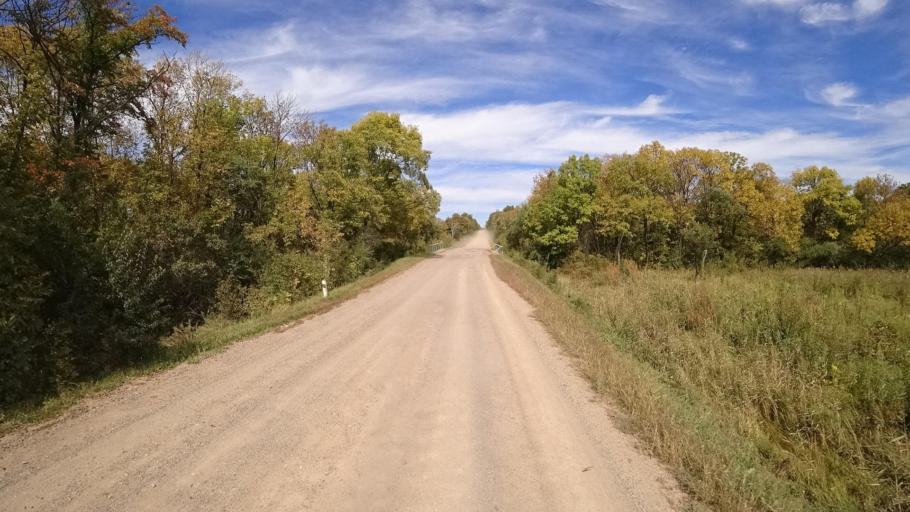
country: RU
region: Primorskiy
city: Yakovlevka
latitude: 44.6200
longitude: 133.5975
